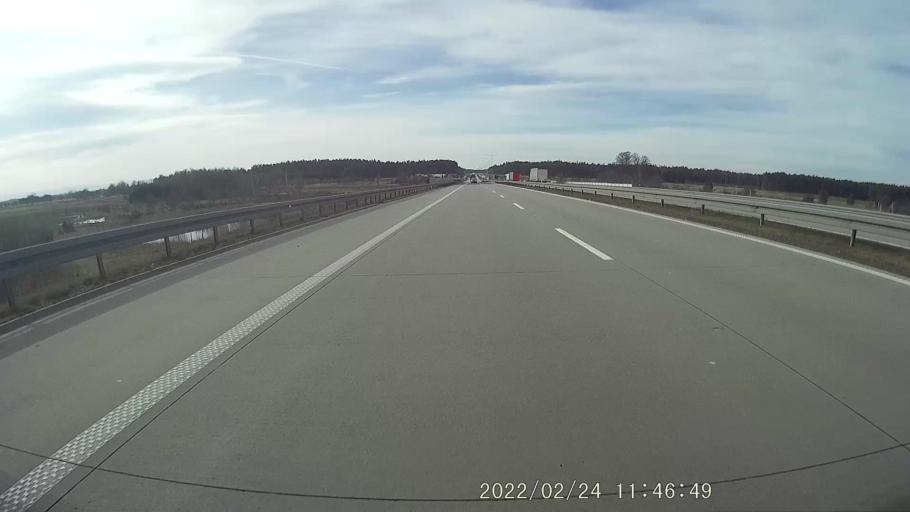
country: PL
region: Lower Silesian Voivodeship
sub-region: Powiat polkowicki
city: Radwanice
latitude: 51.5717
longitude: 15.9483
